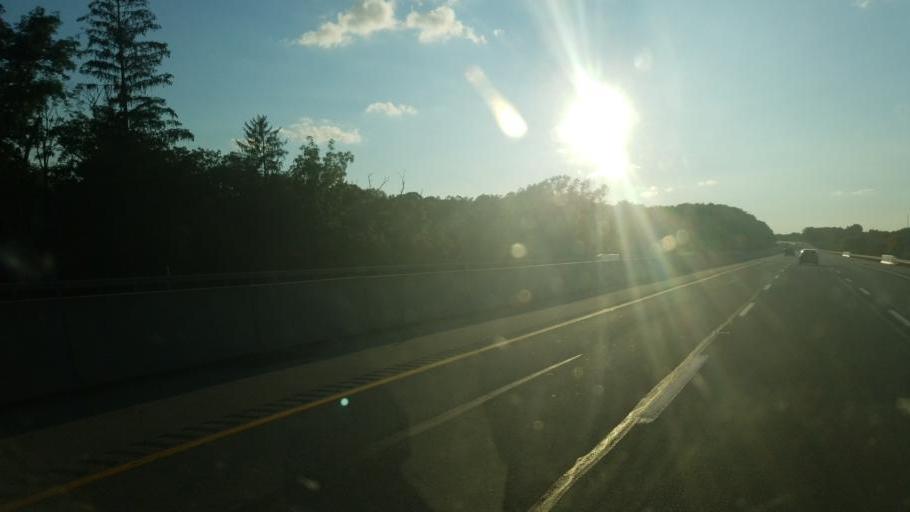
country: US
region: Pennsylvania
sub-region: Lawrence County
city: Bessemer
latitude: 40.8989
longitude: -80.4782
